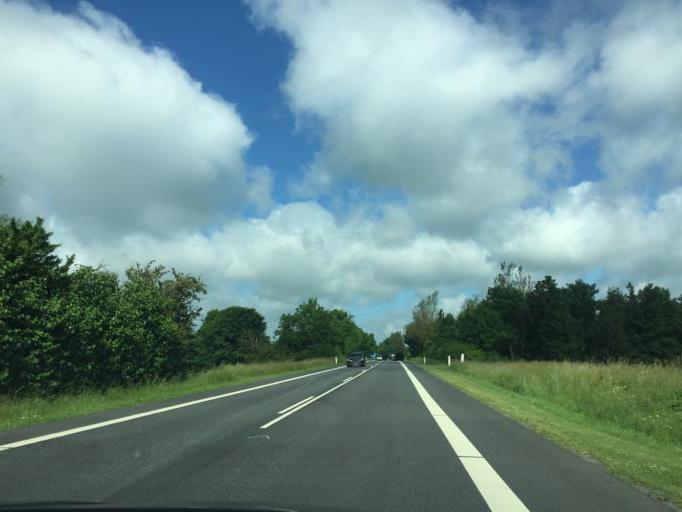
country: DK
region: South Denmark
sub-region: Assens Kommune
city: Arup
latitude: 55.4256
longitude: 10.0239
